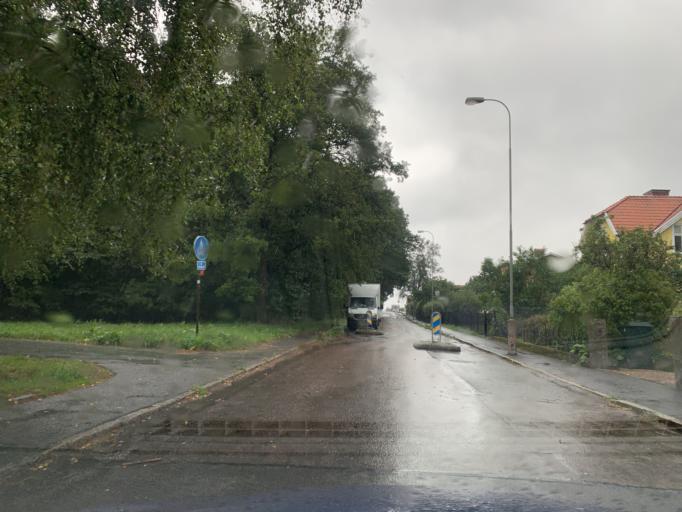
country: SE
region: Vaestra Goetaland
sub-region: Goteborg
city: Goeteborg
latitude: 57.7063
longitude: 12.0151
